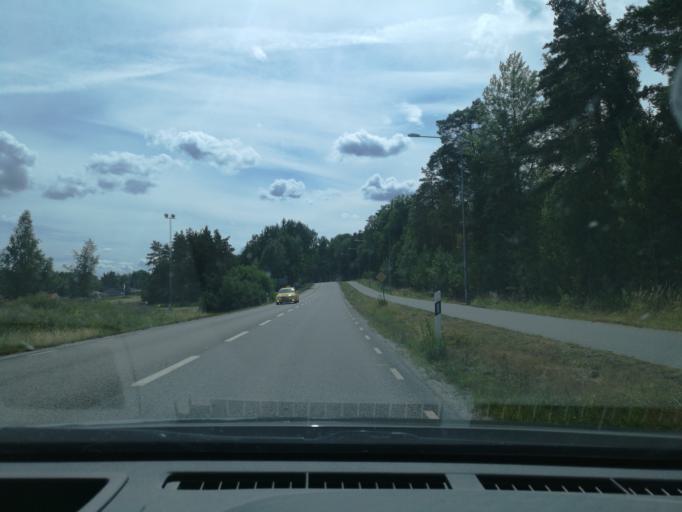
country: SE
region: Stockholm
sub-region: Sigtuna Kommun
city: Rosersberg
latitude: 59.6020
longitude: 17.8824
